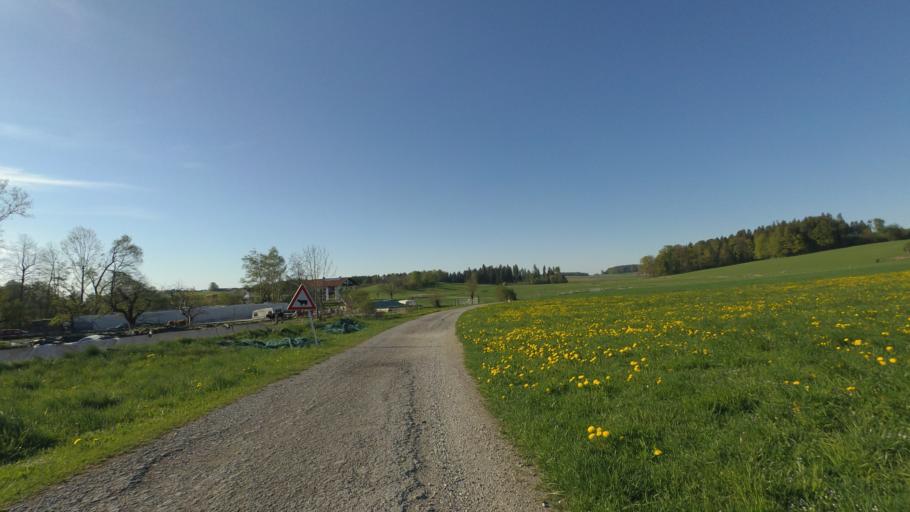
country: DE
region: Bavaria
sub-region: Upper Bavaria
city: Grabenstatt
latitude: 47.8584
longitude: 12.5378
